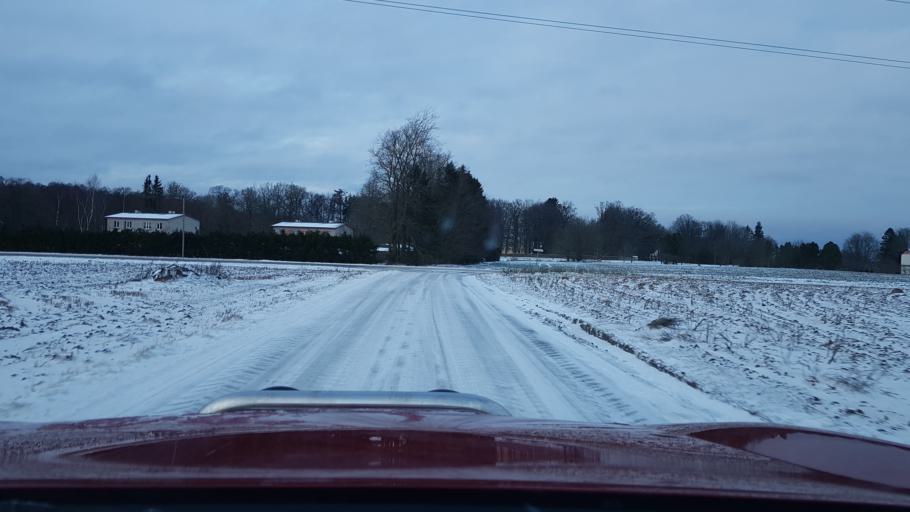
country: EE
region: Harju
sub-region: Maardu linn
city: Maardu
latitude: 59.4250
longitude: 25.0204
